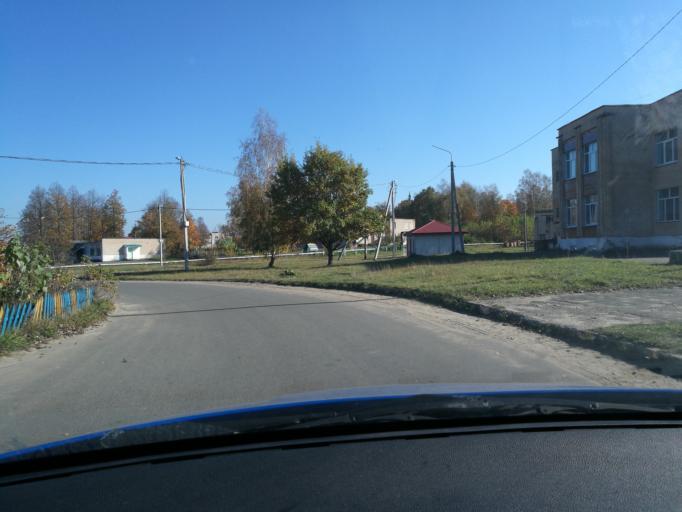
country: BY
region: Minsk
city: Krupki
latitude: 54.1050
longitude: 29.2089
